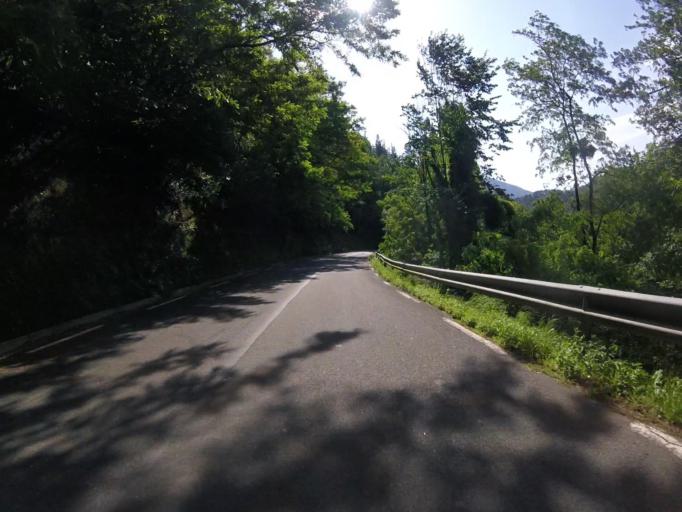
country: ES
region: Basque Country
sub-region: Provincia de Guipuzcoa
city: Hernialde
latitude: 43.1647
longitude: -2.0898
